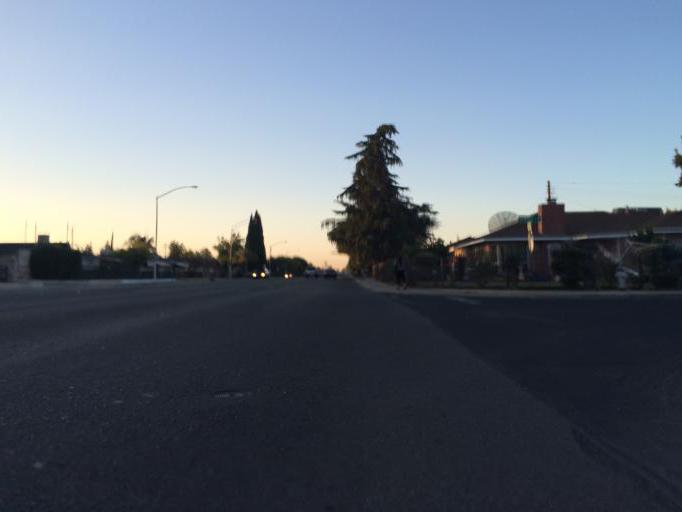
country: US
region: California
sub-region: Fresno County
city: Fresno
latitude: 36.7706
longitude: -119.7546
